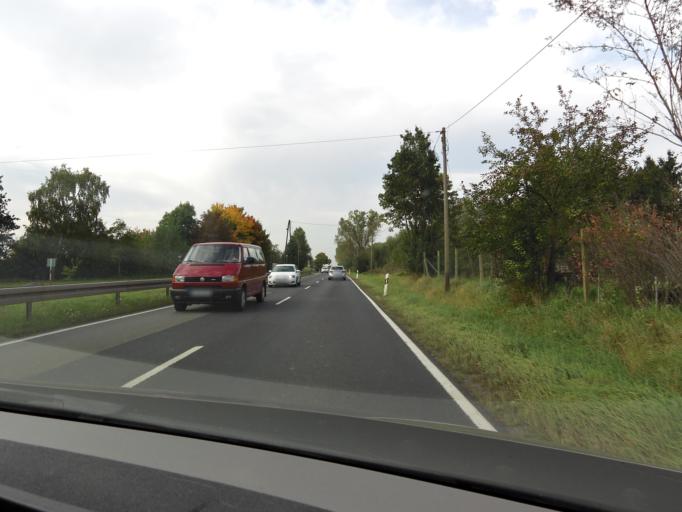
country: DE
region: Thuringia
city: Barchfeld
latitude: 50.7892
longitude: 10.3061
